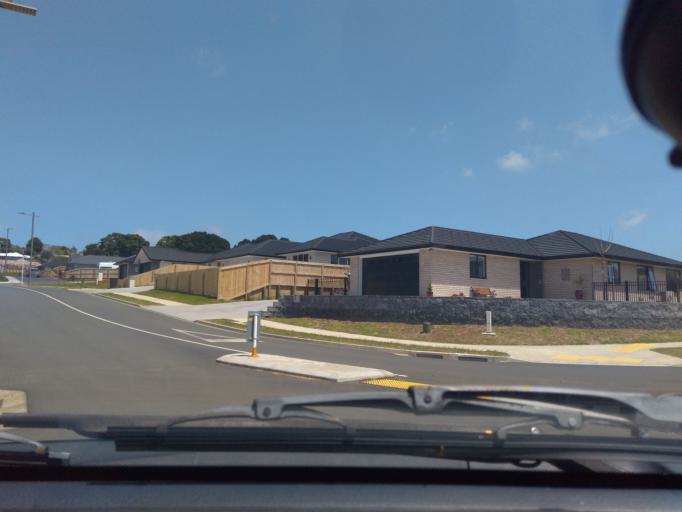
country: NZ
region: Northland
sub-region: Whangarei
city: Whangarei
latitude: -35.6733
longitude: 174.3166
